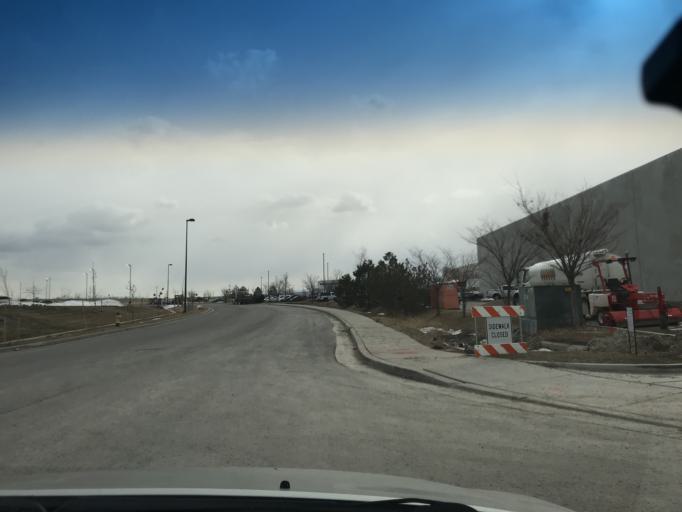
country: US
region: Utah
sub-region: Salt Lake County
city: West Valley City
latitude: 40.7745
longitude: -112.0305
